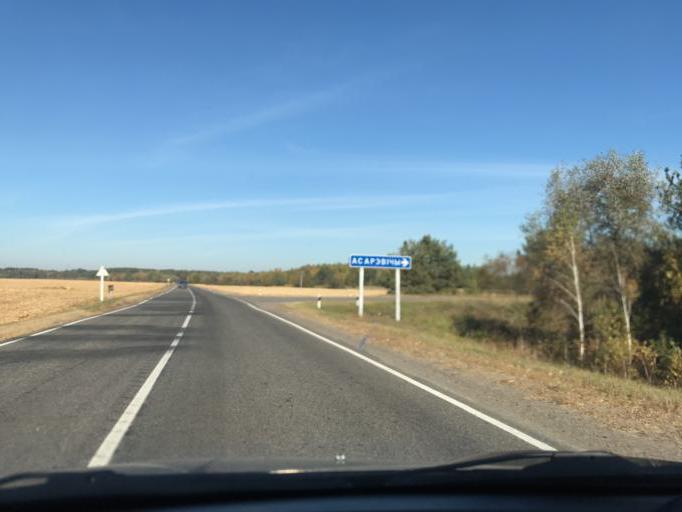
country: UA
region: Chernihiv
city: Lyubech
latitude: 51.5861
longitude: 30.4800
